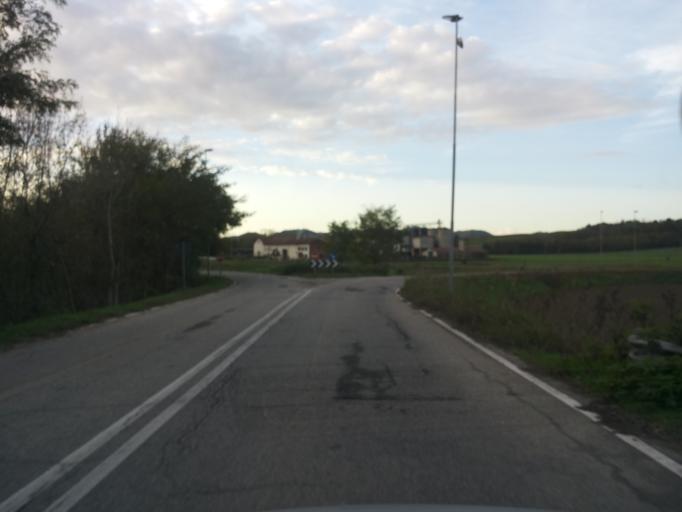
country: IT
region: Piedmont
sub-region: Provincia di Alessandria
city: Cereseto
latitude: 45.1135
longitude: 8.3228
